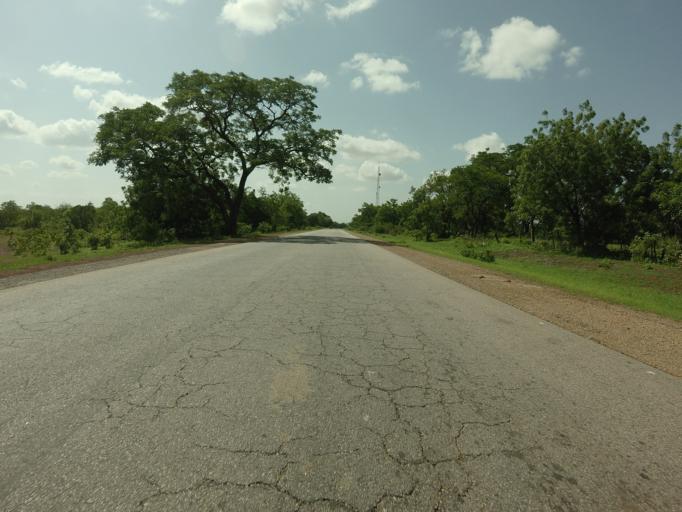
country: GH
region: Northern
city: Savelugu
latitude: 9.8145
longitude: -0.8618
